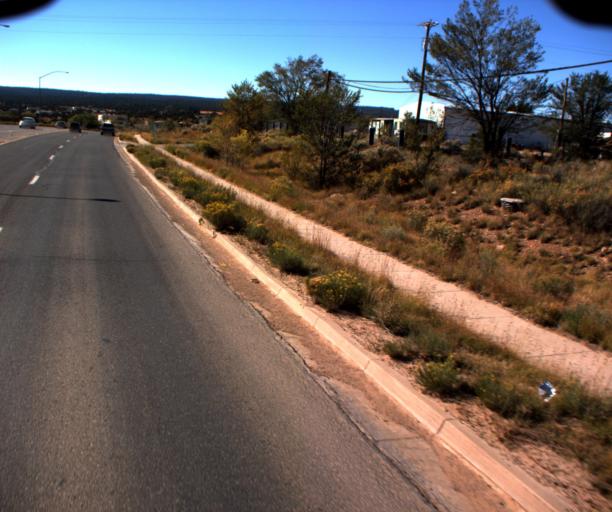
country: US
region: Arizona
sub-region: Apache County
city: Saint Michaels
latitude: 35.6554
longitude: -109.0991
